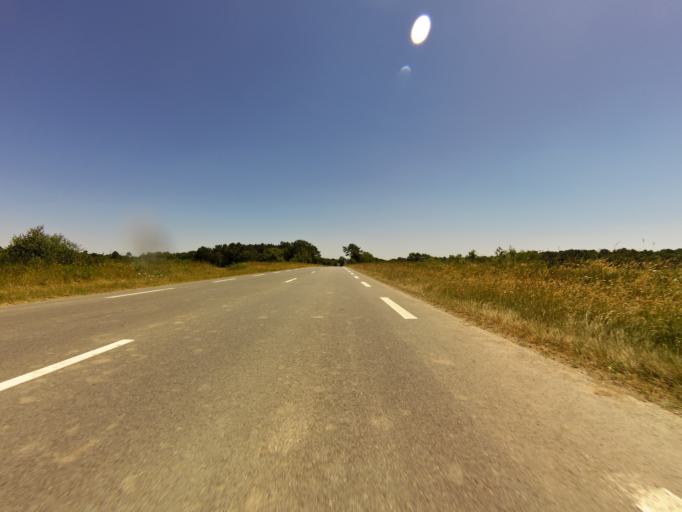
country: FR
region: Brittany
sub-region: Departement du Morbihan
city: Peaule
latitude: 47.5281
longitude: -2.3845
